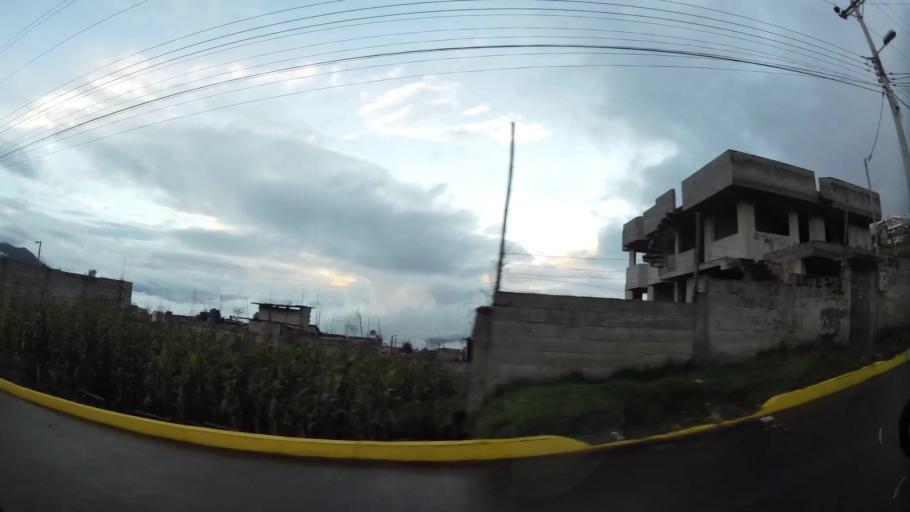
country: EC
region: Pichincha
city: Quito
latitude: -0.0960
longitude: -78.5312
